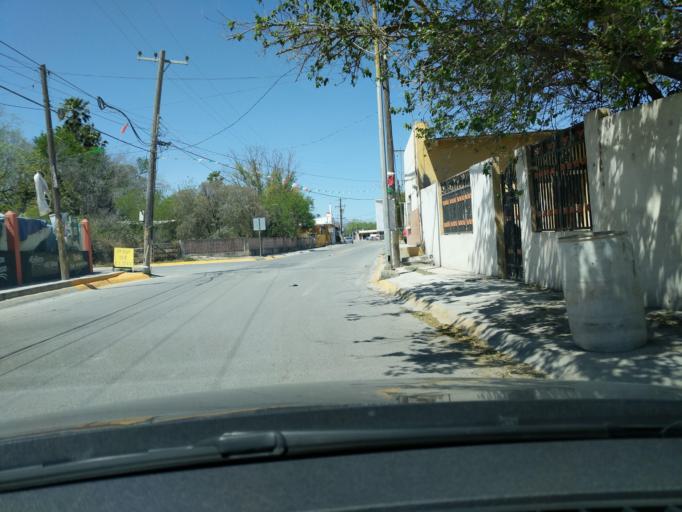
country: MX
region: Nuevo Leon
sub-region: Apodaca
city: Artemio Trevino
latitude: 25.8129
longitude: -100.1502
